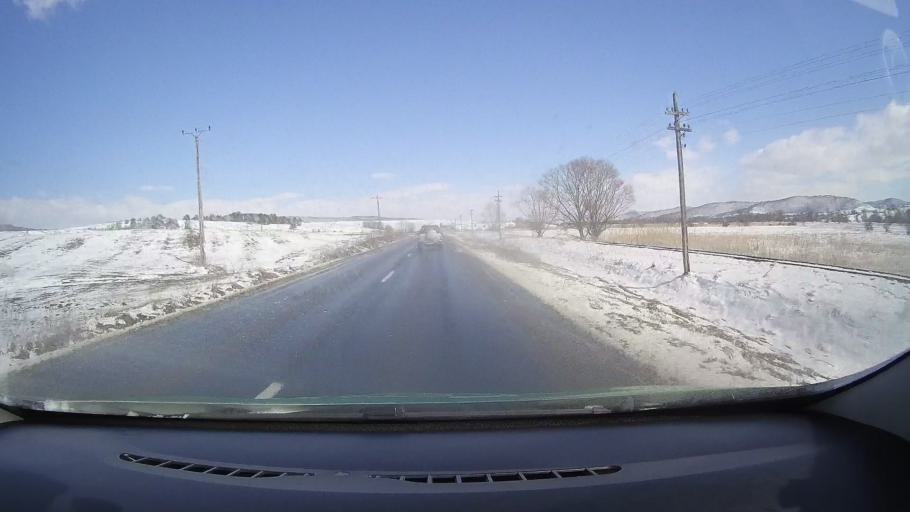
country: RO
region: Sibiu
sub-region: Comuna Rosia
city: Rosia
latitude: 45.8084
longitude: 24.3588
